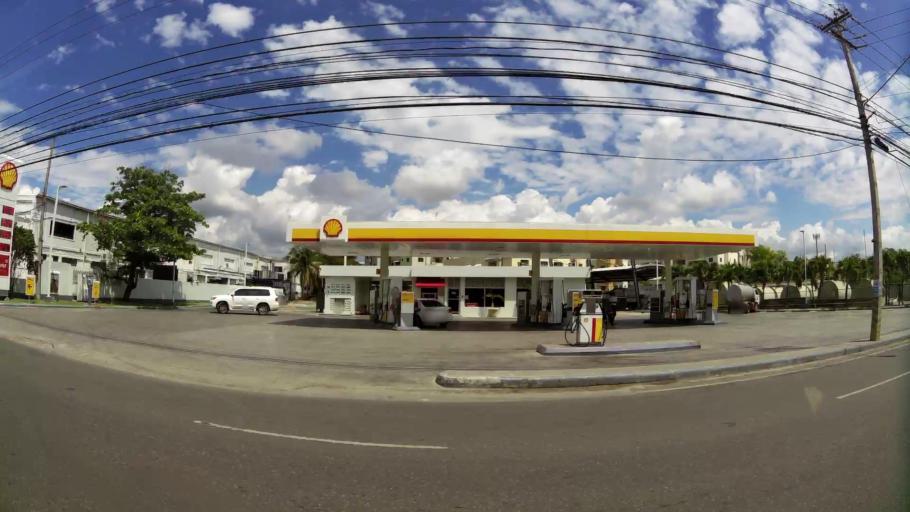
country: DO
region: Santiago
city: Santiago de los Caballeros
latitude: 19.4554
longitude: -70.6630
